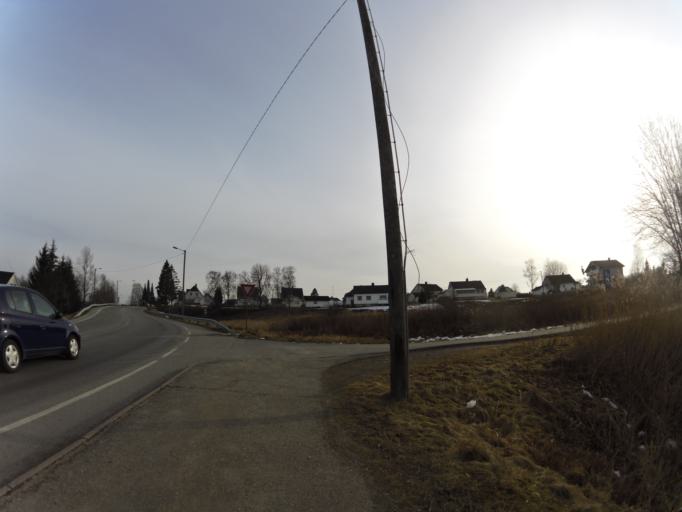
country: NO
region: Ostfold
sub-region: Sarpsborg
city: Sarpsborg
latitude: 59.2704
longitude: 11.0196
